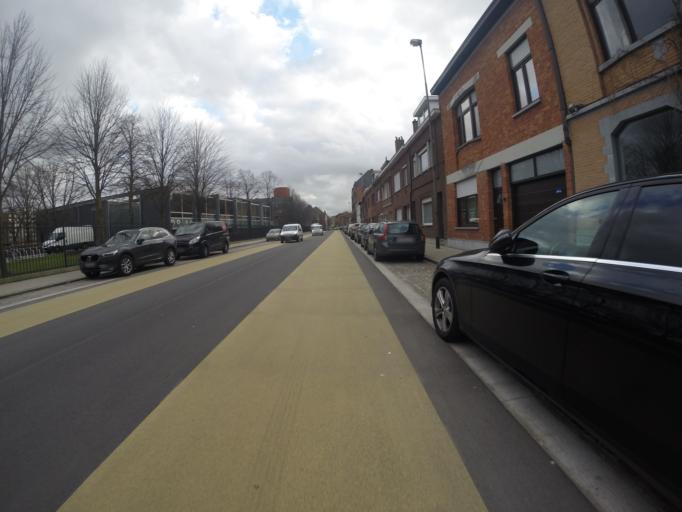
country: BE
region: Flanders
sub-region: Provincie Oost-Vlaanderen
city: Gent
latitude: 51.0758
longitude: 3.7147
